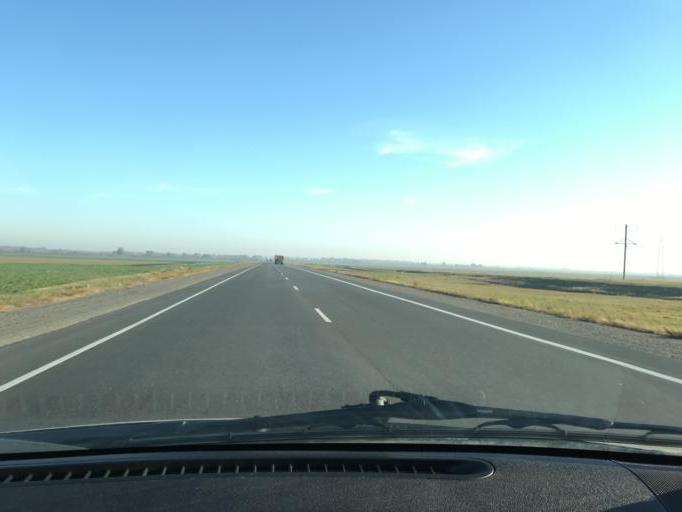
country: BY
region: Brest
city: Asnyezhytsy
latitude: 52.2007
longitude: 26.1115
